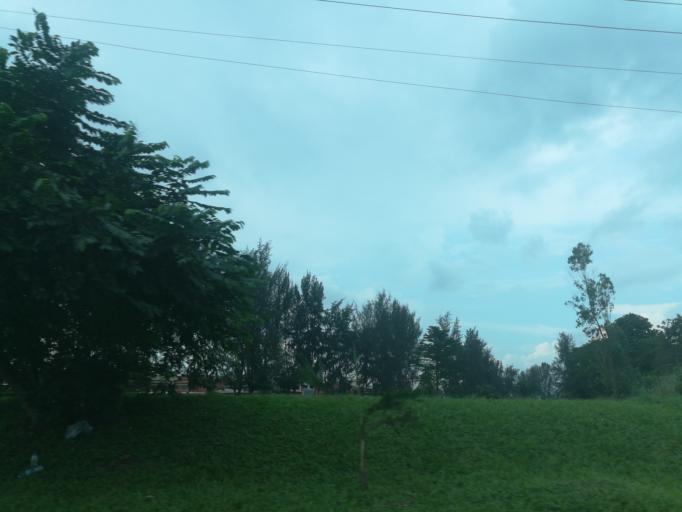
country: NG
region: Lagos
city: Ikorodu
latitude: 6.6353
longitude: 3.5246
